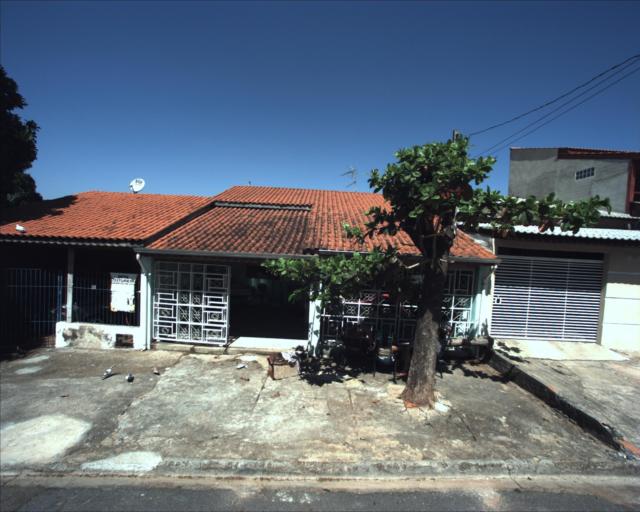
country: BR
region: Sao Paulo
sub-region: Sorocaba
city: Sorocaba
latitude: -23.4723
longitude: -47.4829
